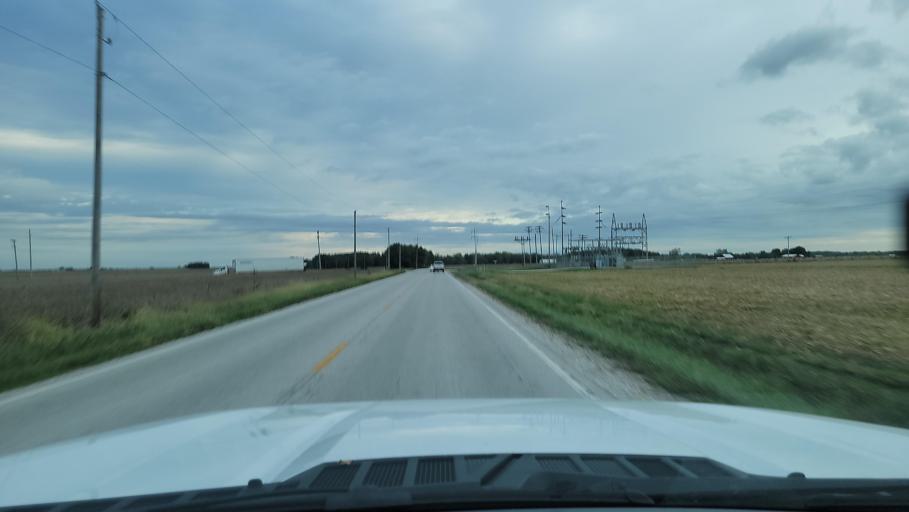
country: US
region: Illinois
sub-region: Schuyler County
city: Rushville
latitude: 40.1446
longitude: -90.5583
